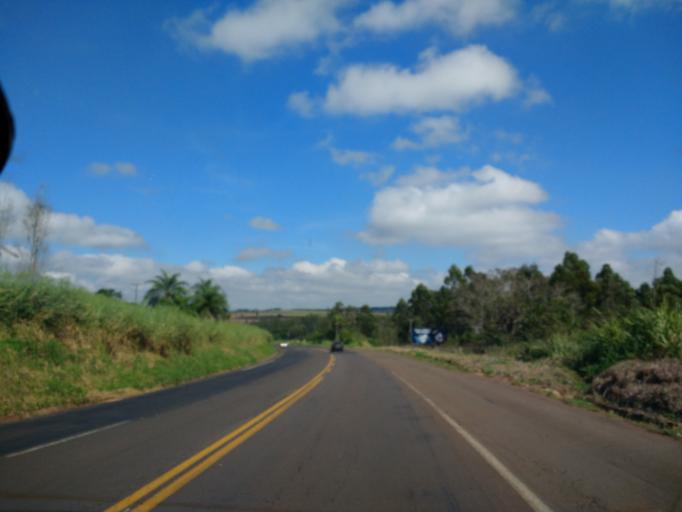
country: BR
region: Parana
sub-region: Umuarama
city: Umuarama
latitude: -23.7722
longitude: -53.2521
